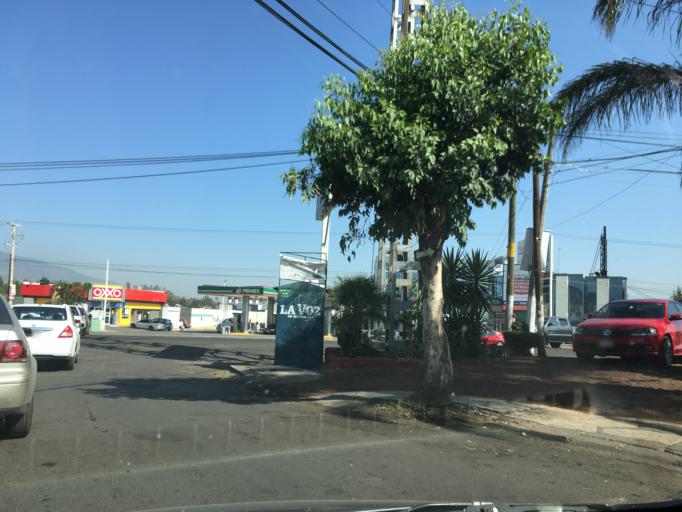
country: MX
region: Michoacan
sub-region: Morelia
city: Morelos
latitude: 19.6766
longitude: -101.2300
